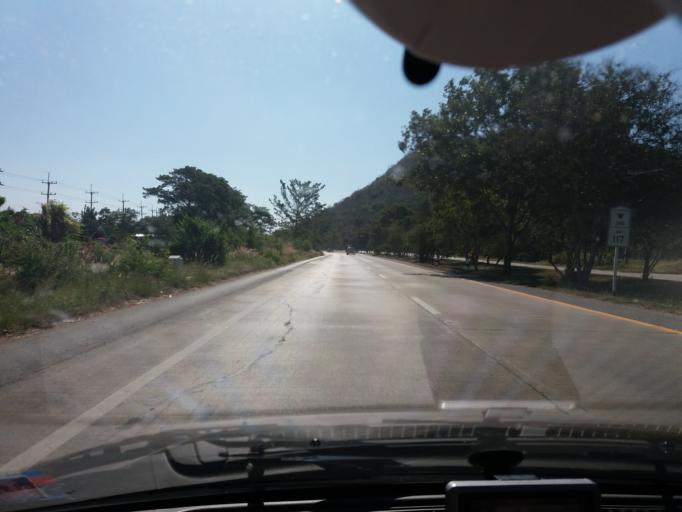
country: TH
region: Suphan Buri
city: Doem Bang Nang Buat
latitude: 14.8449
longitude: 100.1023
